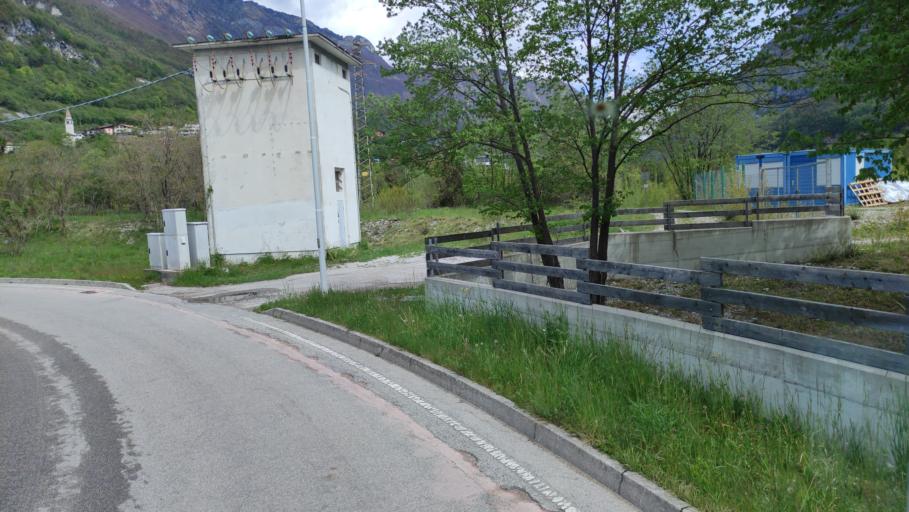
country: IT
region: Veneto
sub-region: Provincia di Belluno
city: Longarone
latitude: 46.2585
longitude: 12.3039
